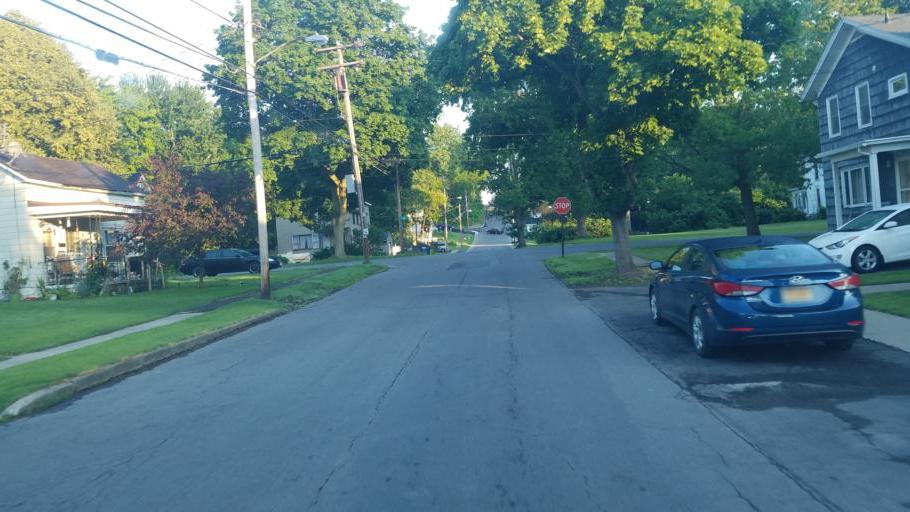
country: US
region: New York
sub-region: Wayne County
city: Clyde
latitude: 43.0870
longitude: -76.8711
